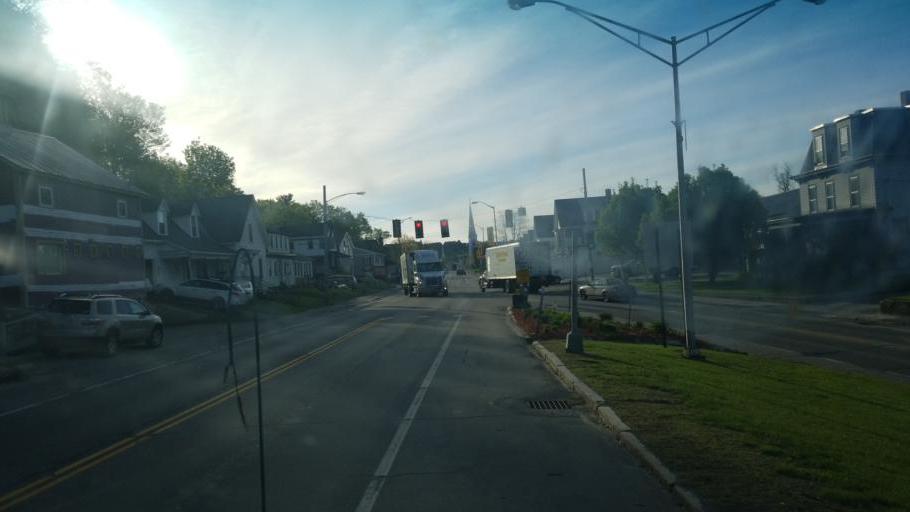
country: US
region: New Hampshire
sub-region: Grafton County
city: Littleton
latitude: 44.3086
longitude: -71.7818
